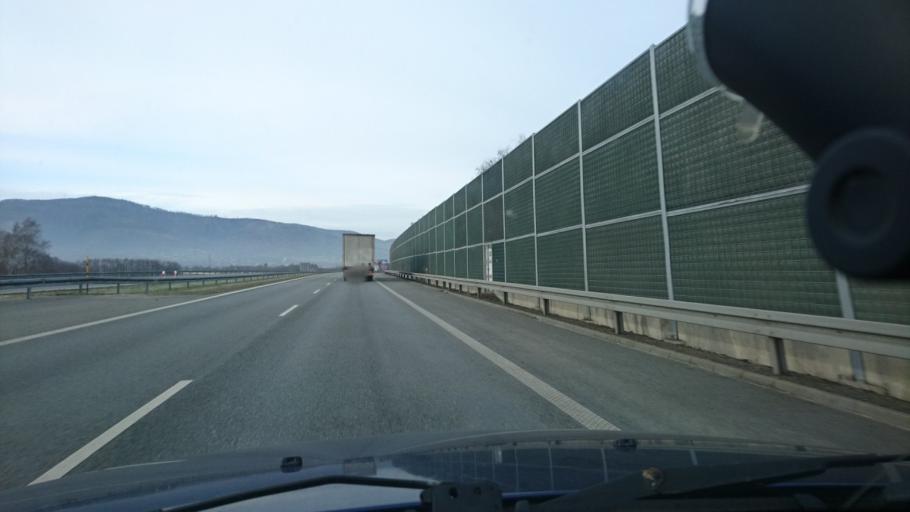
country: PL
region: Silesian Voivodeship
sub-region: Powiat bielski
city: Rybarzowice
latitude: 49.7415
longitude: 19.0992
